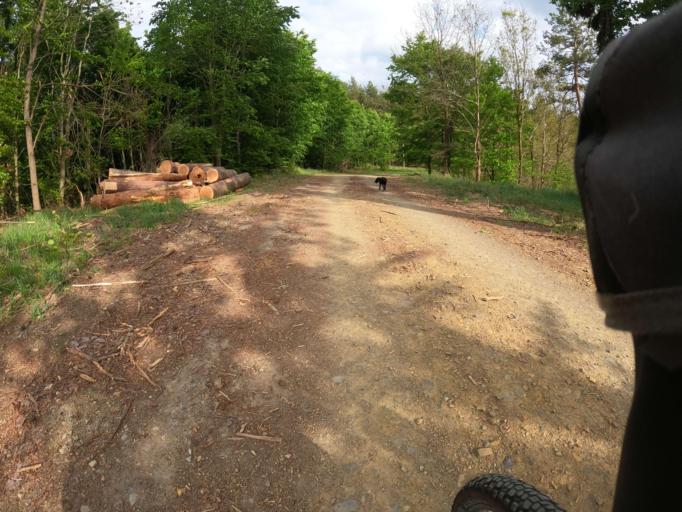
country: PL
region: West Pomeranian Voivodeship
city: Trzcinsko Zdroj
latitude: 52.9148
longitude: 14.6918
